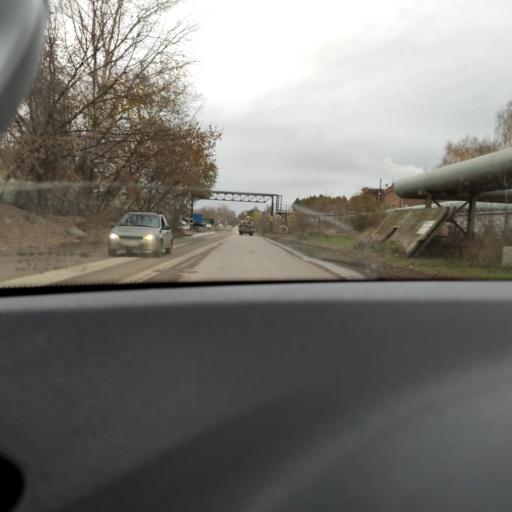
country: RU
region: Samara
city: Smyshlyayevka
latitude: 53.2037
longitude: 50.2973
